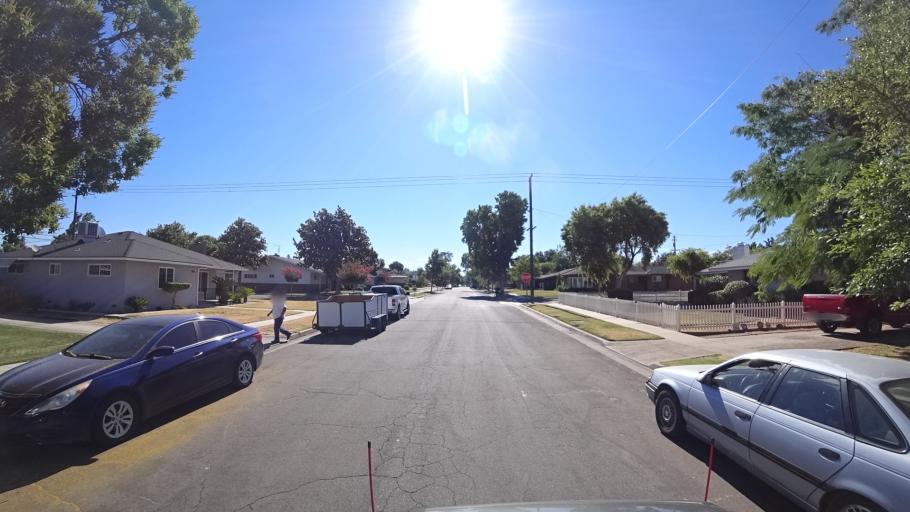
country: US
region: California
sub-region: Fresno County
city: Fresno
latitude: 36.7757
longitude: -119.8226
